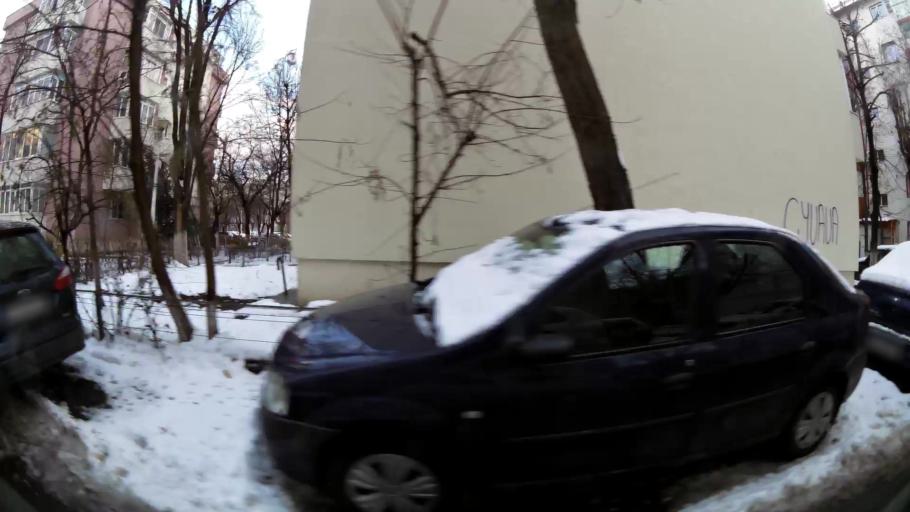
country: RO
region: Ilfov
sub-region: Comuna Fundeni-Dobroesti
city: Fundeni
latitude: 44.4449
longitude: 26.1693
